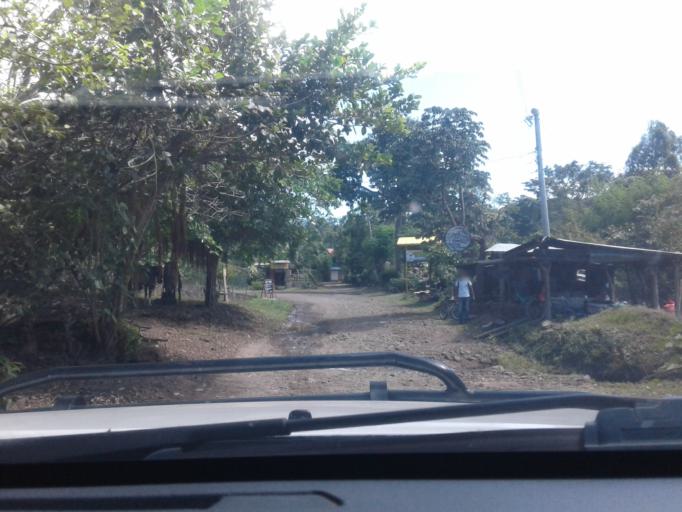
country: NI
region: Rivas
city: Altagracia
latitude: 11.4428
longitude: -85.5608
